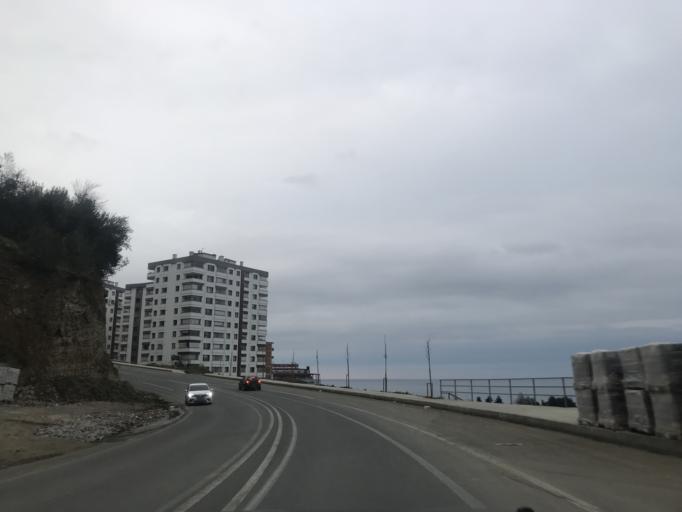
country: TR
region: Trabzon
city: Akcaabat
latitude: 41.0041
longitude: 39.6267
